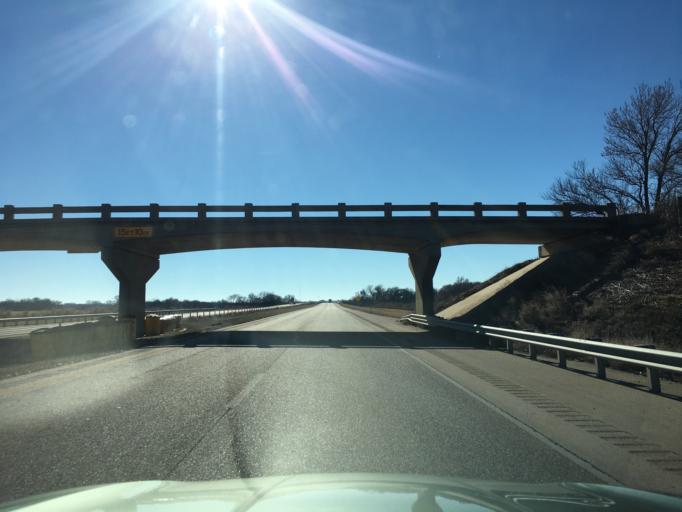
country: US
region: Oklahoma
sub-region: Kay County
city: Blackwell
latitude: 36.9132
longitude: -97.3520
